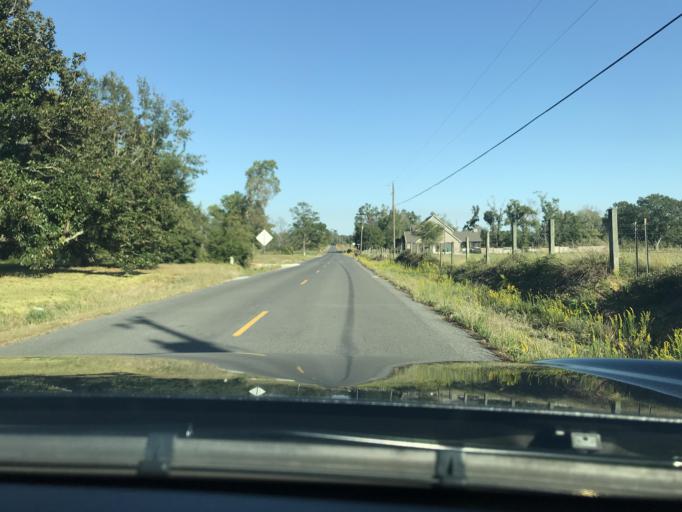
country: US
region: Louisiana
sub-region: Calcasieu Parish
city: Westlake
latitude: 30.3153
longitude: -93.2682
